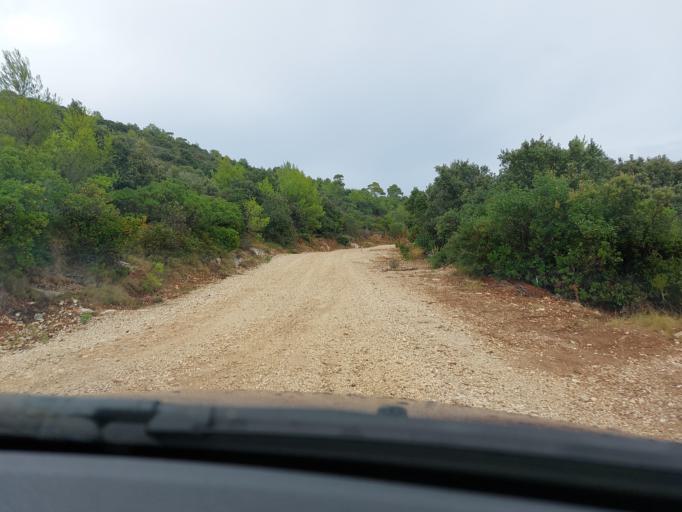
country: HR
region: Dubrovacko-Neretvanska
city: Smokvica
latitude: 42.7428
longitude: 16.9131
